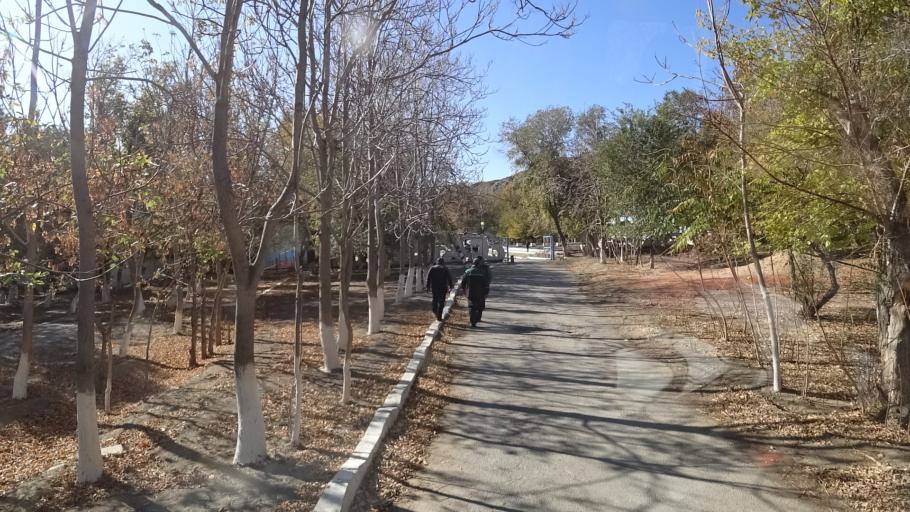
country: UZ
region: Navoiy
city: Karmana Shahri
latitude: 40.2956
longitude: 65.6044
